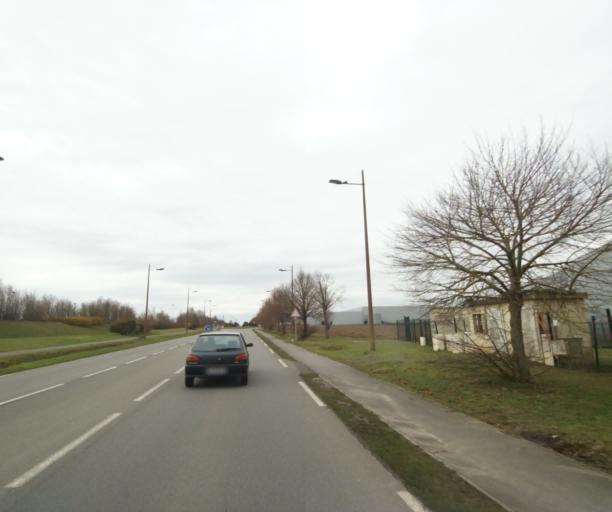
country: FR
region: Nord-Pas-de-Calais
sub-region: Departement du Nord
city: Onnaing
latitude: 50.3703
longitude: 3.6109
